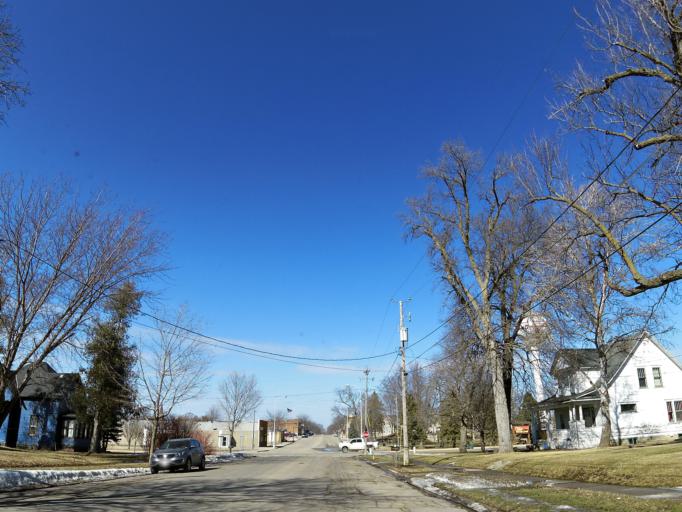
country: US
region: Minnesota
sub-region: Waseca County
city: New Richland
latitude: 43.8911
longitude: -93.4939
